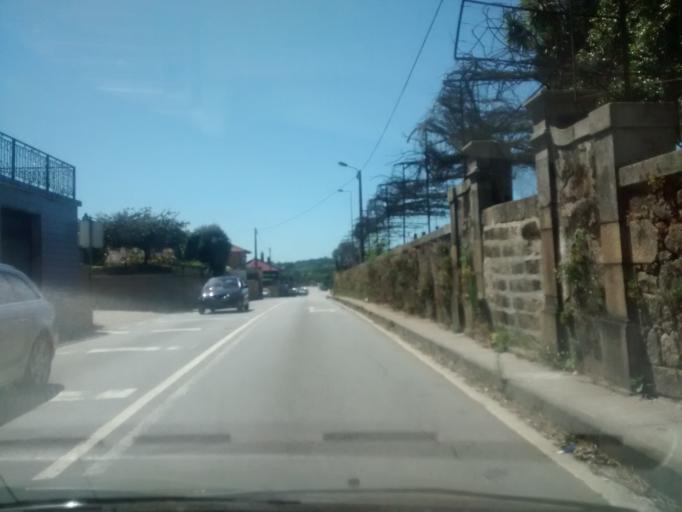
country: PT
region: Braga
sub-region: Braga
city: Oliveira
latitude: 41.5335
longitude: -8.4963
